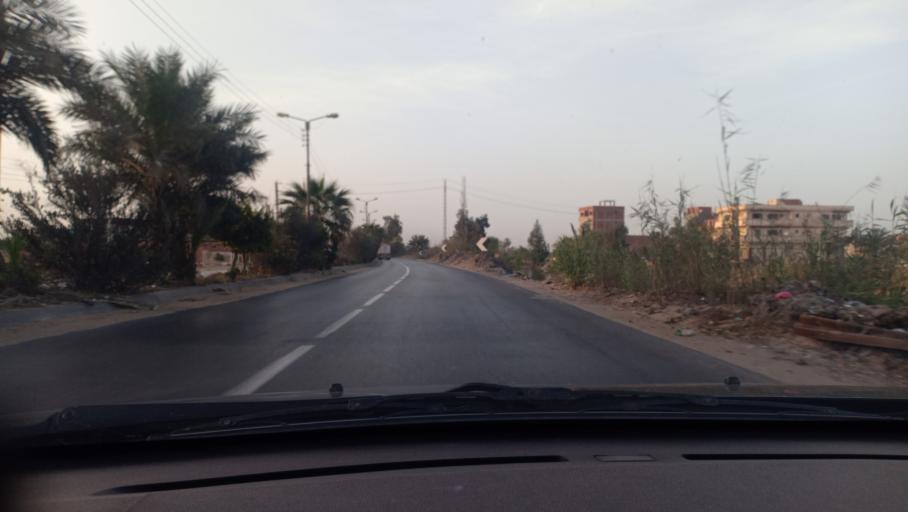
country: EG
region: Muhafazat al Gharbiyah
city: Zifta
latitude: 30.6431
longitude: 31.2822
